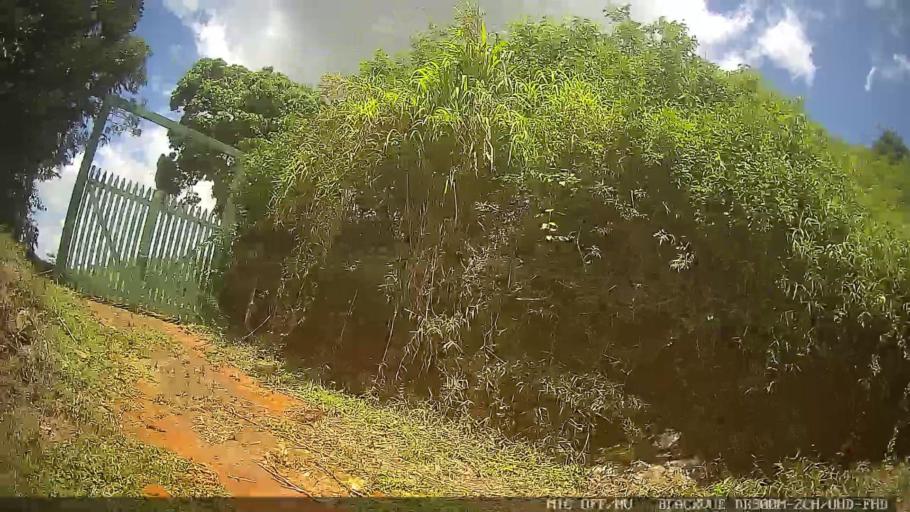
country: BR
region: Minas Gerais
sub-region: Extrema
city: Extrema
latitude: -22.8876
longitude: -46.3098
